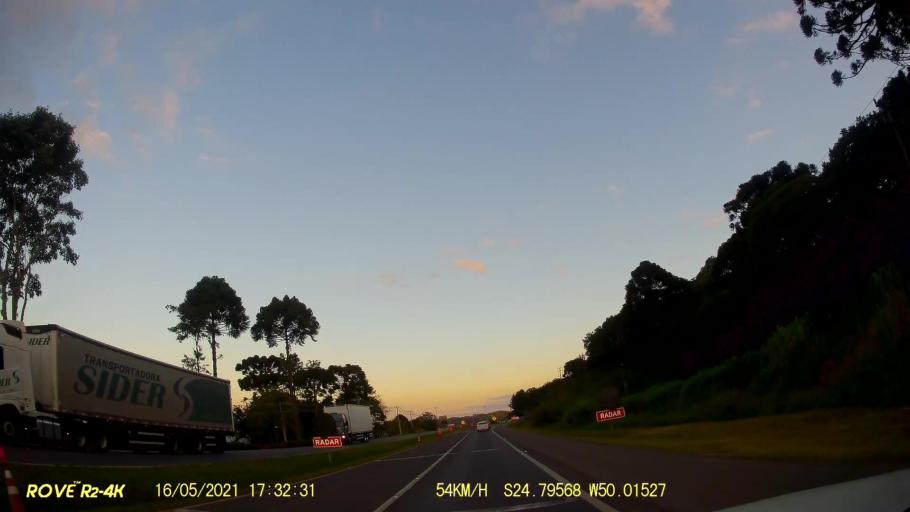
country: BR
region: Parana
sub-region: Castro
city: Castro
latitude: -24.7958
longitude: -50.0152
